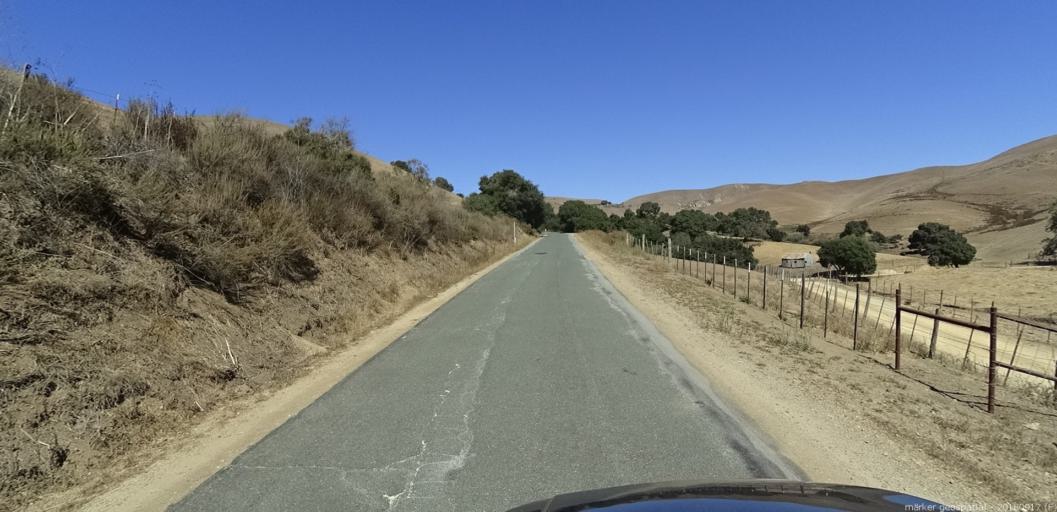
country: US
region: California
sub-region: San Benito County
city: San Juan Bautista
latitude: 36.8002
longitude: -121.5802
